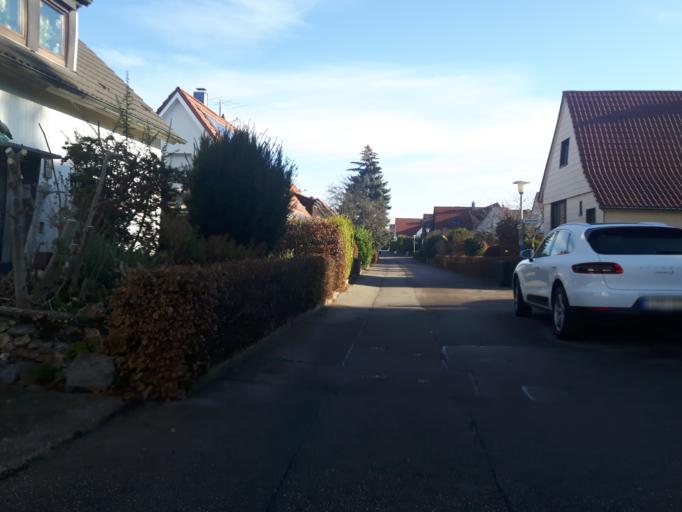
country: DE
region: Baden-Wuerttemberg
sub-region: Regierungsbezirk Stuttgart
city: Heilbronn
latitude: 49.1501
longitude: 9.1873
